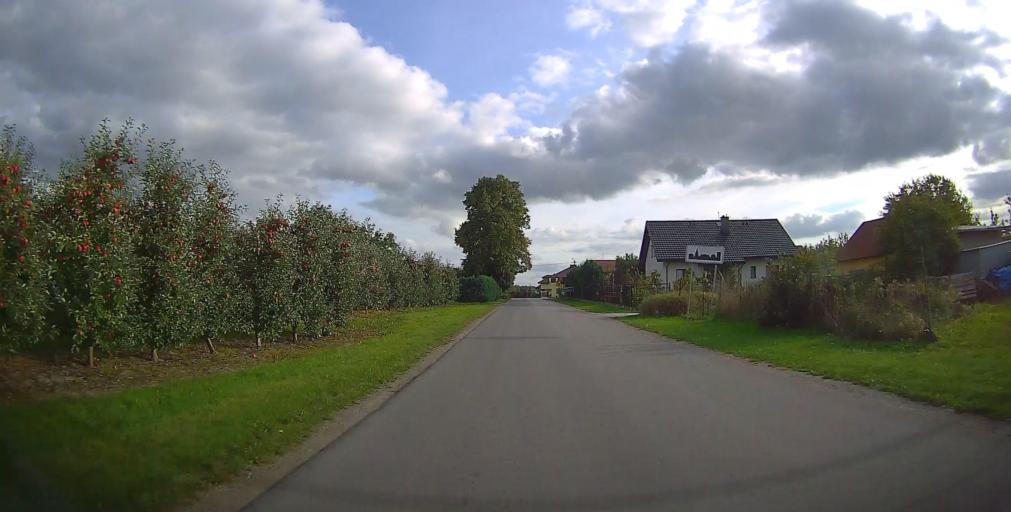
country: PL
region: Masovian Voivodeship
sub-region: Powiat bialobrzeski
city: Promna
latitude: 51.7418
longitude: 20.9649
